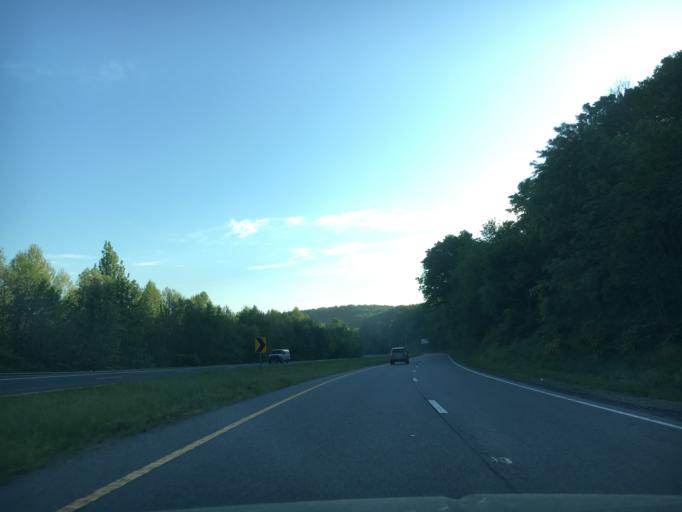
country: US
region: Virginia
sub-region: Campbell County
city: Rustburg
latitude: 37.3125
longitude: -79.1072
